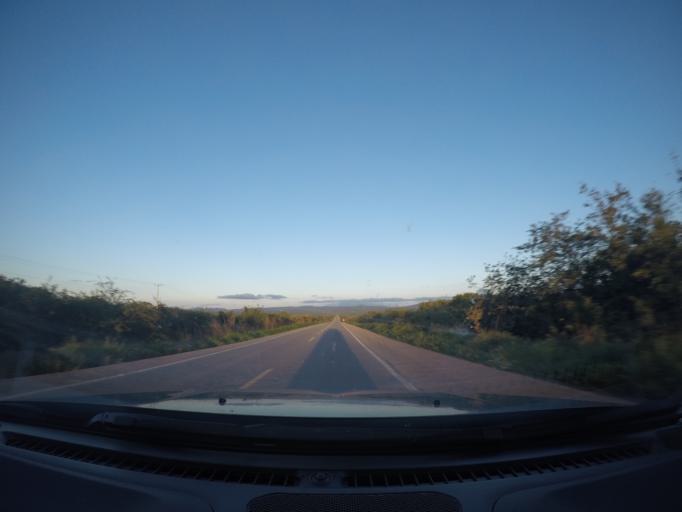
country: BR
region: Bahia
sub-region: Seabra
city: Seabra
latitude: -12.4068
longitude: -41.9601
